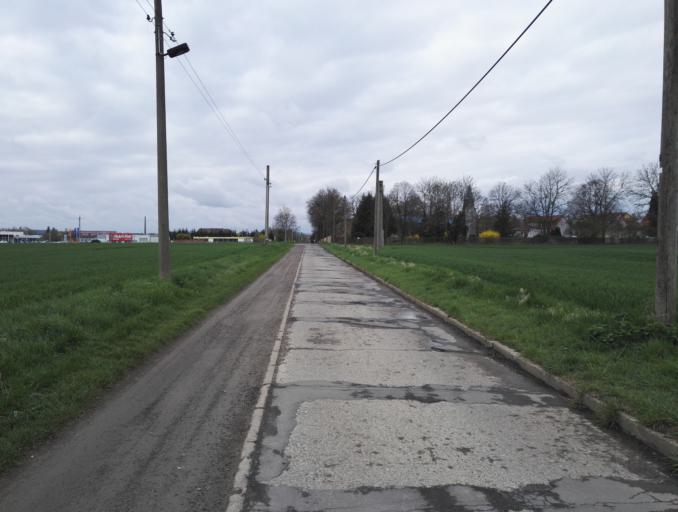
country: DE
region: Saxony-Anhalt
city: Halberstadt
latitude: 51.9051
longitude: 11.0801
